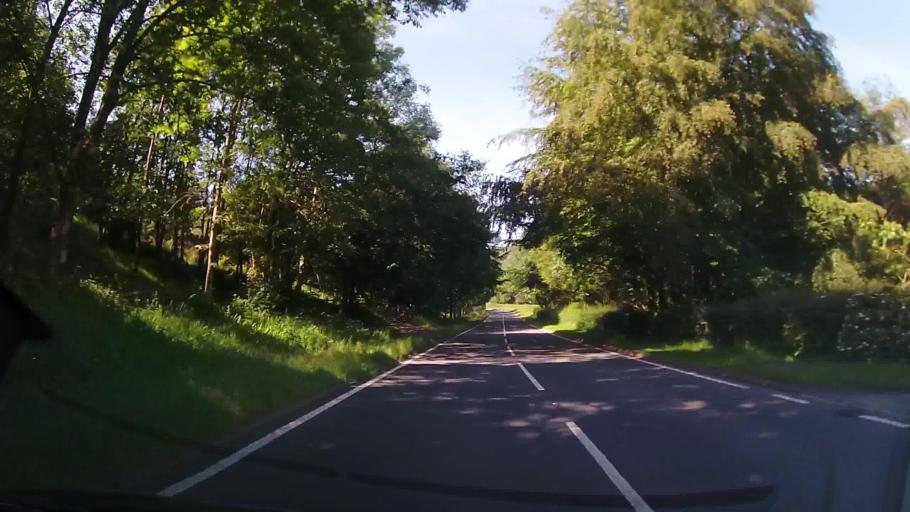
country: GB
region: Wales
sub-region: Gwynedd
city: Corris
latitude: 52.6738
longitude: -3.7025
